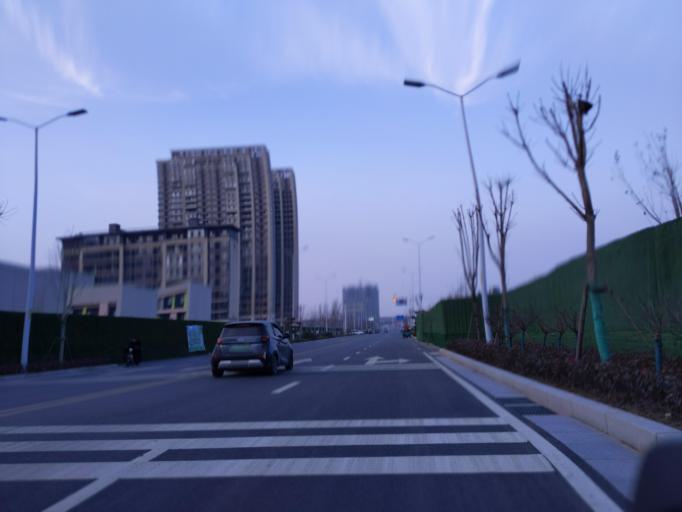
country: CN
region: Henan Sheng
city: Puyang
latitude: 35.8068
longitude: 115.0112
